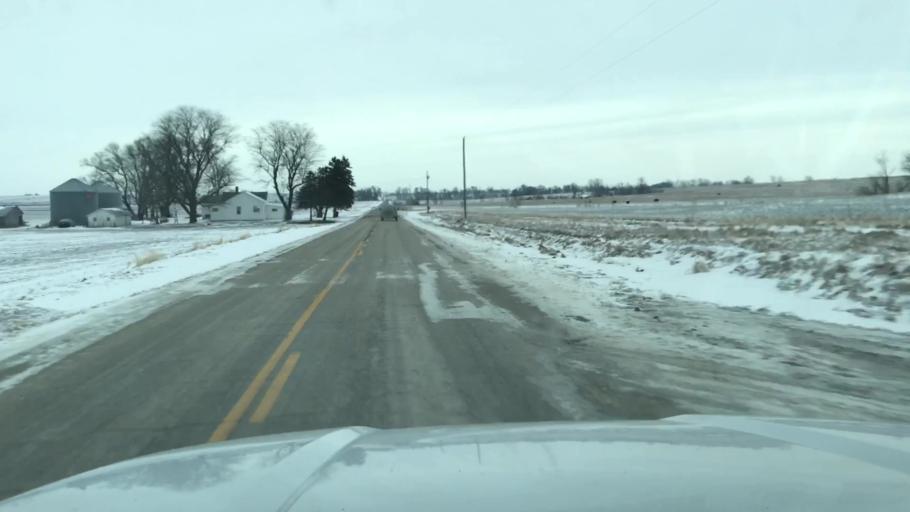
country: US
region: Missouri
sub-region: Holt County
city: Oregon
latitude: 40.1157
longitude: -95.0226
